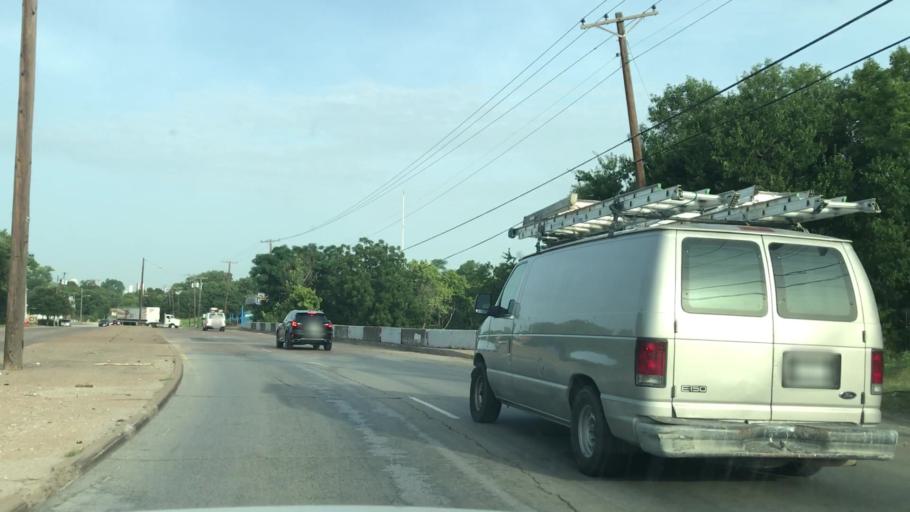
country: US
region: Texas
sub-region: Dallas County
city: Dallas
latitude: 32.7837
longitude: -96.7284
